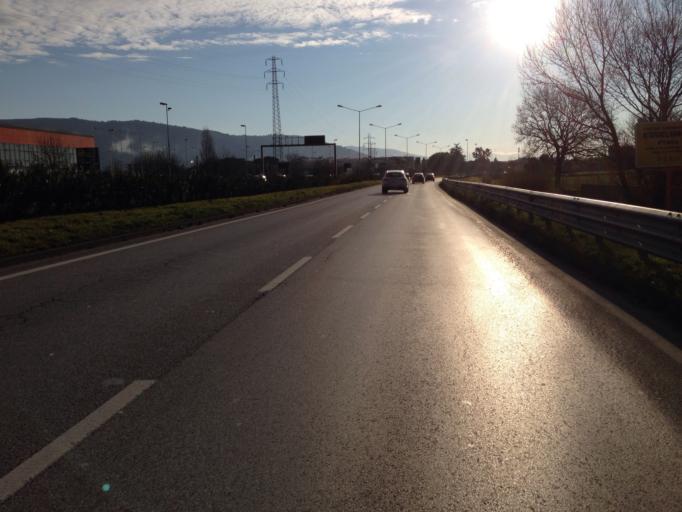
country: IT
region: Tuscany
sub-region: Provincia di Prato
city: Prato
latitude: 43.8769
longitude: 11.0731
